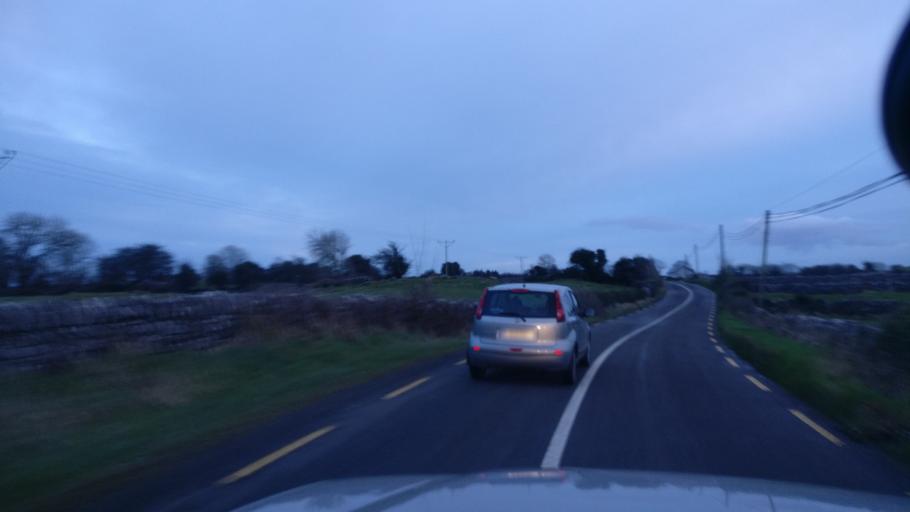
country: IE
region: Connaught
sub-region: County Galway
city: Loughrea
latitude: 53.2176
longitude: -8.6178
